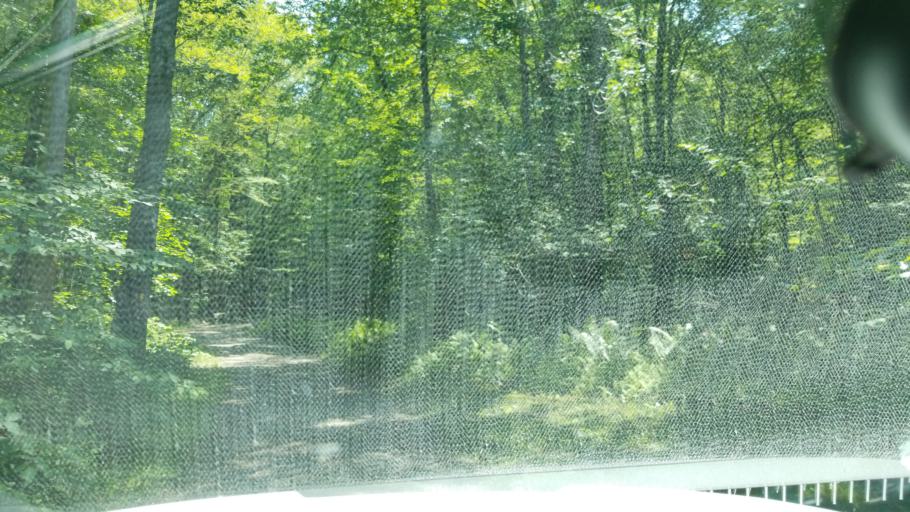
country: US
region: Connecticut
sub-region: Litchfield County
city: New Preston
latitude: 41.6952
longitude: -73.2800
